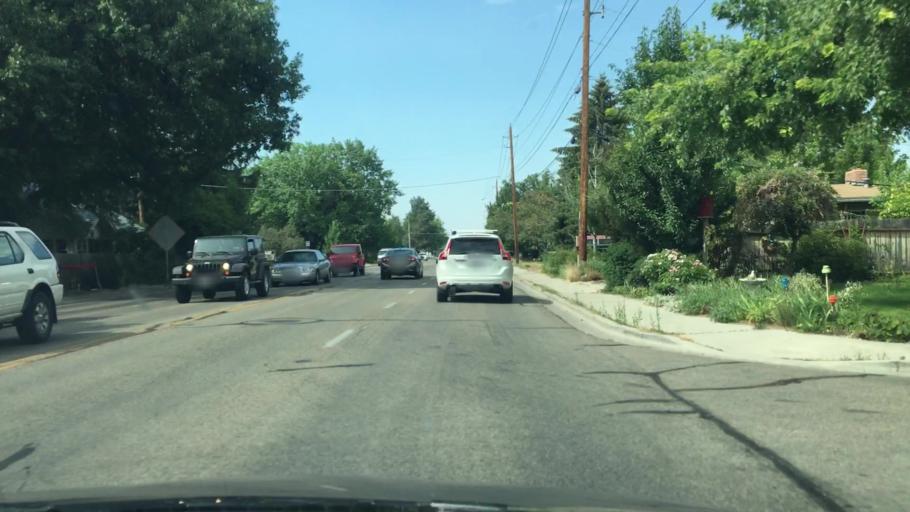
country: US
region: Idaho
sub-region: Ada County
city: Garden City
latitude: 43.6298
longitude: -116.2742
